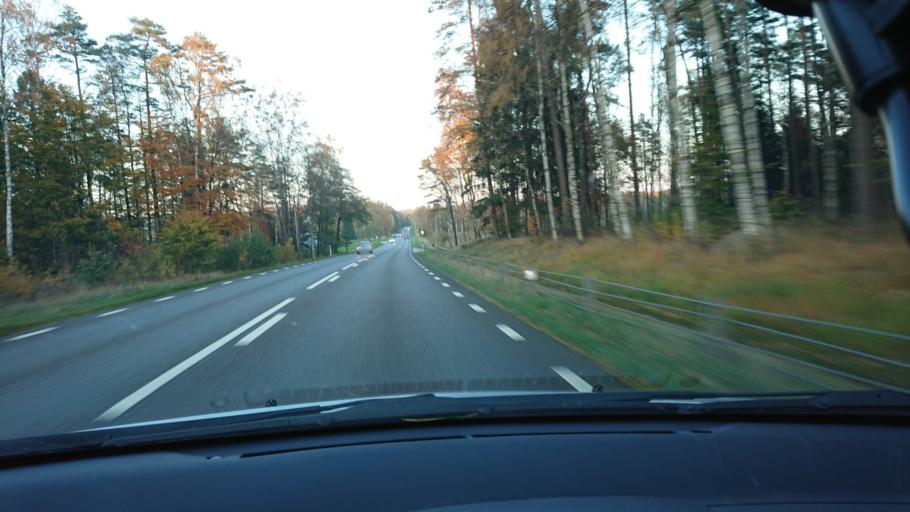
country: SE
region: Halland
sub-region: Halmstads Kommun
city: Oskarstrom
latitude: 56.7149
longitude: 13.1061
